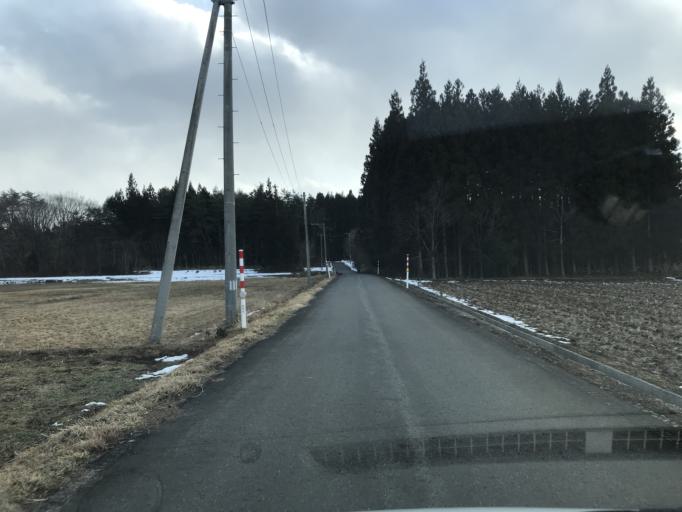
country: JP
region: Iwate
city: Mizusawa
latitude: 39.1094
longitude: 140.9818
